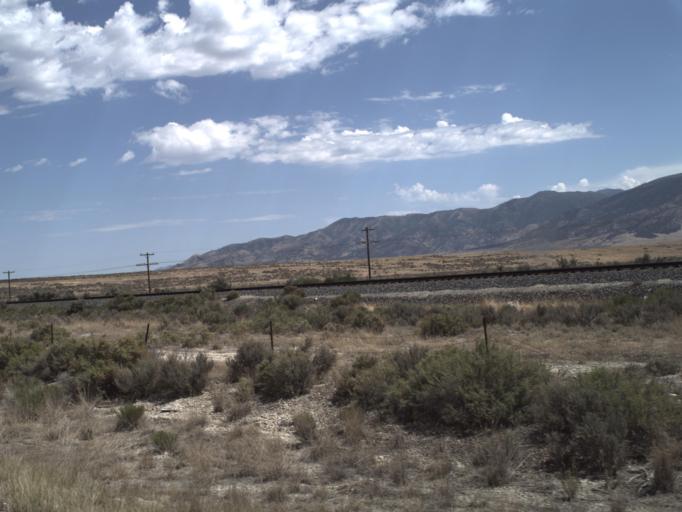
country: US
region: Utah
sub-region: Tooele County
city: Tooele
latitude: 40.3455
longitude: -112.4112
